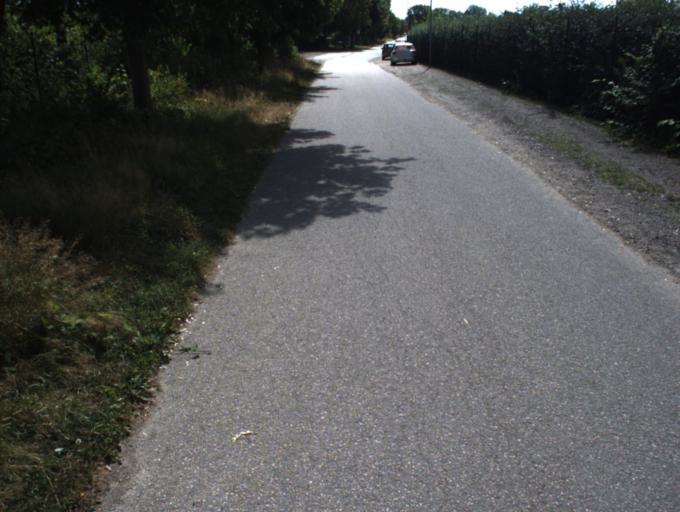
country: SE
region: Skane
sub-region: Helsingborg
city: Helsingborg
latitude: 56.0573
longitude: 12.7315
